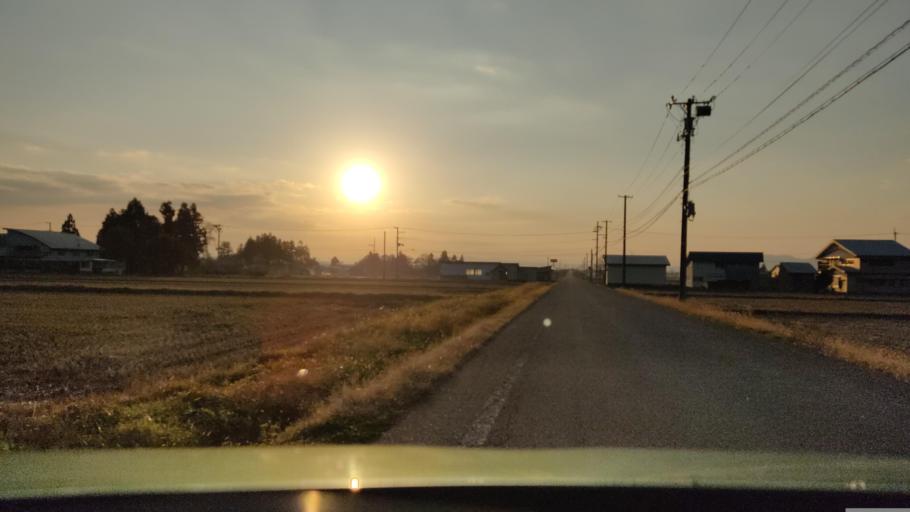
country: JP
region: Akita
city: Omagari
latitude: 39.4524
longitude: 140.5858
